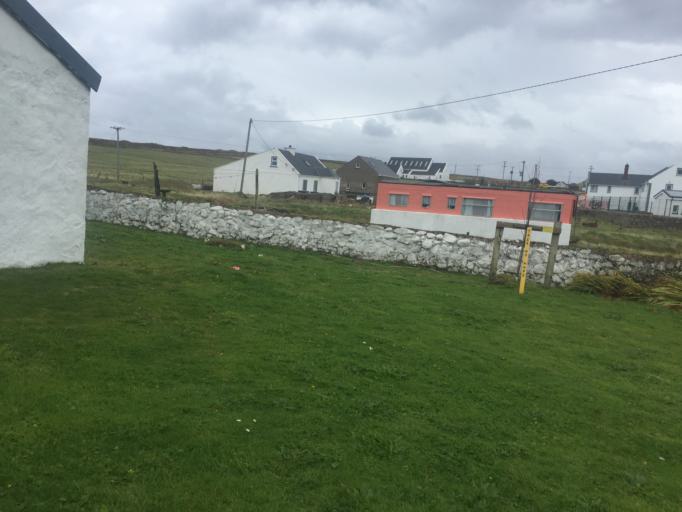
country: IE
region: Ulster
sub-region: County Donegal
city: Derrybeg
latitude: 55.2656
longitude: -8.2255
